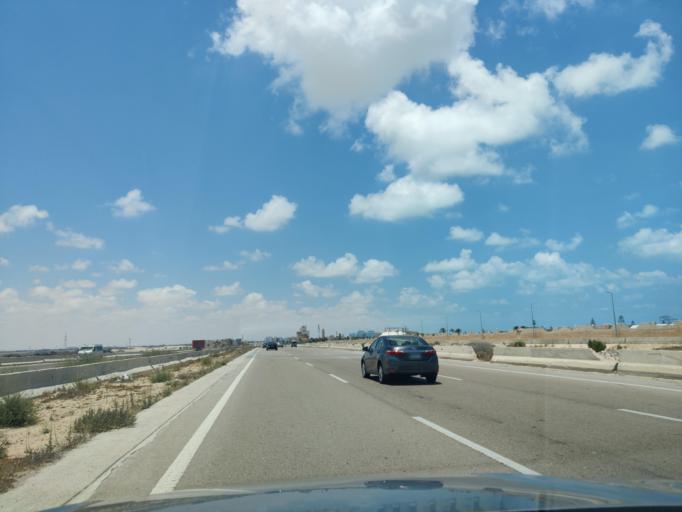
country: EG
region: Muhafazat Matruh
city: Al `Alamayn
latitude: 30.8146
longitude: 29.0408
